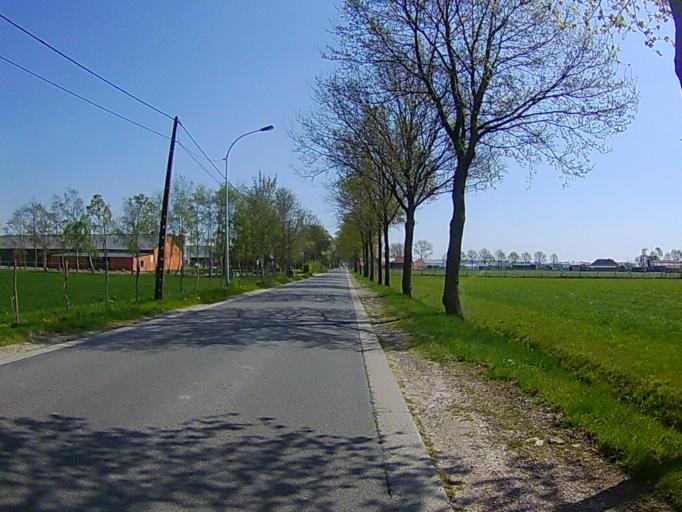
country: BE
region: Flanders
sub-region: Provincie Antwerpen
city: Hoogstraten
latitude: 51.3819
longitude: 4.7442
